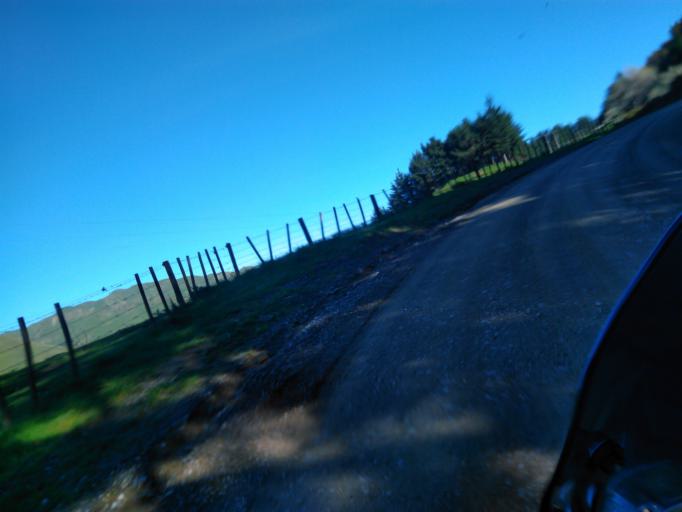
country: NZ
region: Gisborne
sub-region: Gisborne District
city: Gisborne
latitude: -38.4076
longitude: 177.6817
